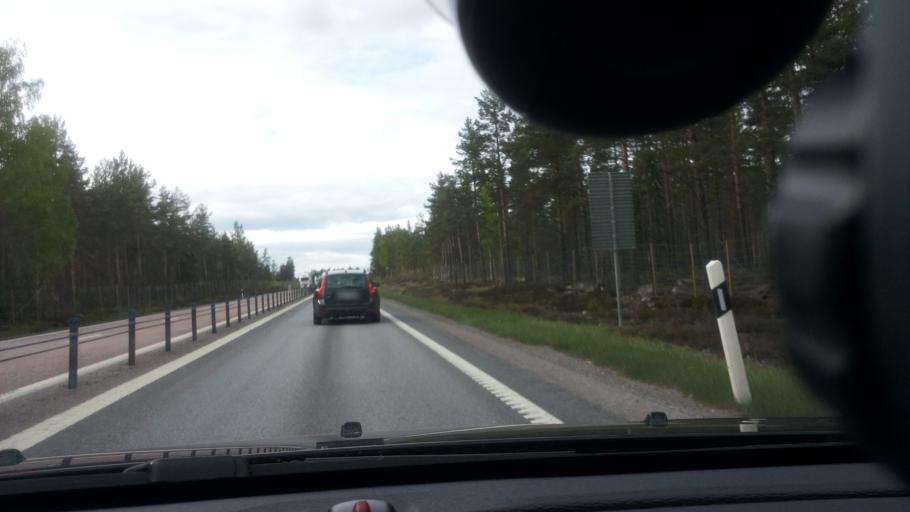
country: SE
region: Gaevleborg
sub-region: Gavle Kommun
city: Norrsundet
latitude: 60.9760
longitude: 17.0210
